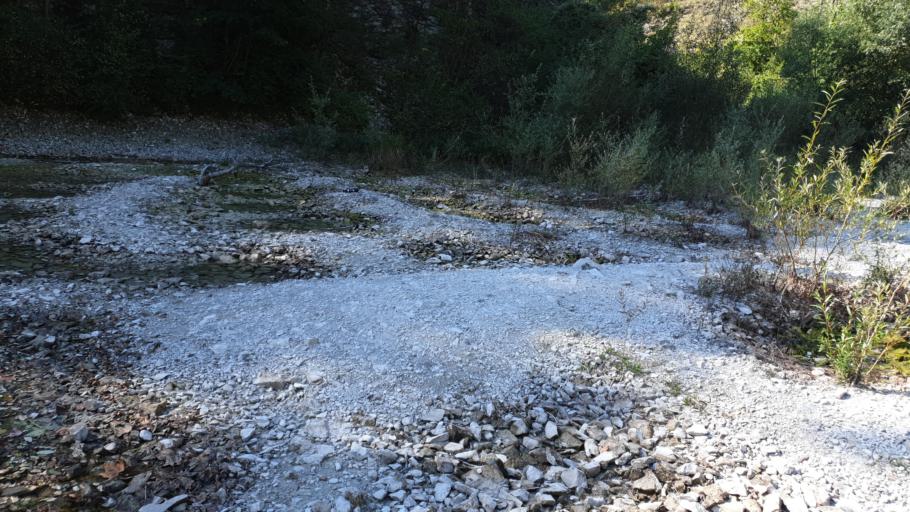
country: DE
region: North Rhine-Westphalia
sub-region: Regierungsbezirk Munster
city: Tecklenburg
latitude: 52.2040
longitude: 7.8353
